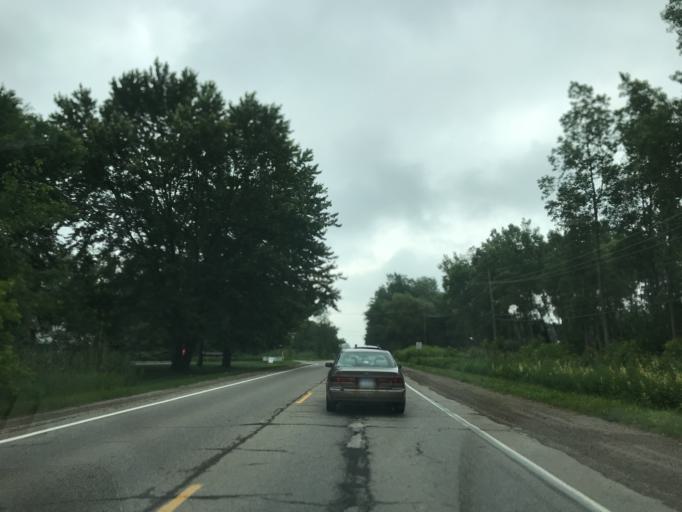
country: US
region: Michigan
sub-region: Oakland County
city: Wixom
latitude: 42.5018
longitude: -83.5701
